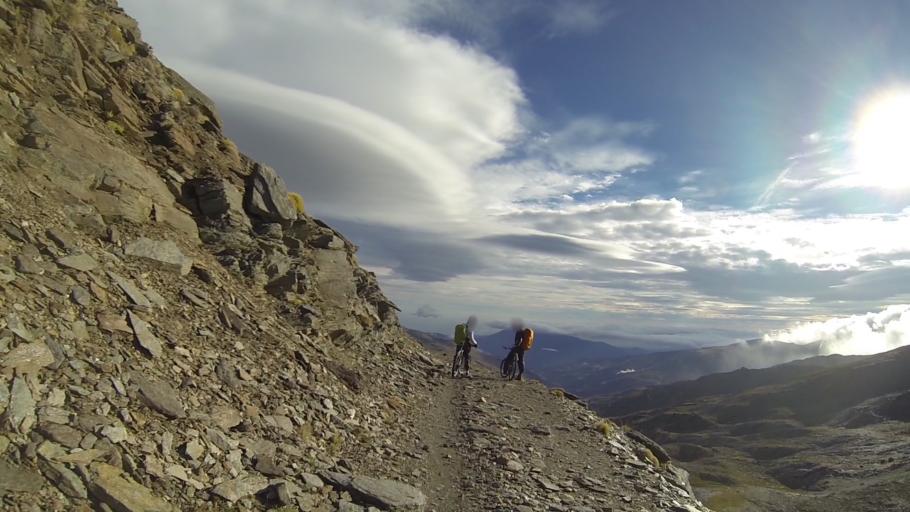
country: ES
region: Andalusia
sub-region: Provincia de Granada
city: Trevelez
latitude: 37.0462
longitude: -3.3206
